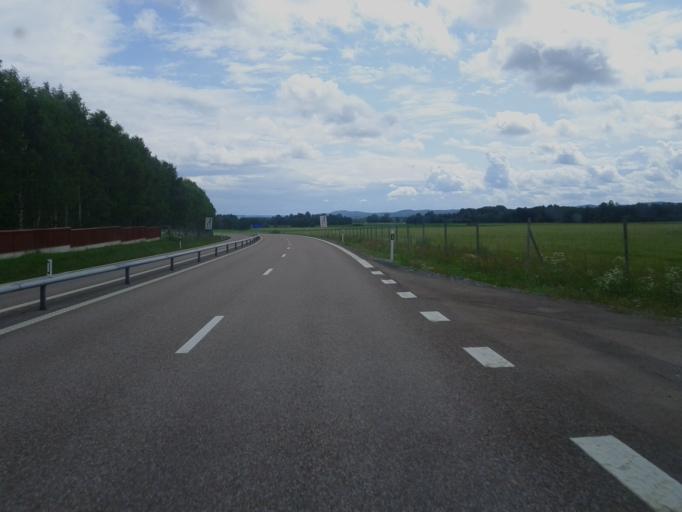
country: SE
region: Dalarna
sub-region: Saters Kommun
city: Saeter
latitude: 60.3320
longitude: 15.8322
